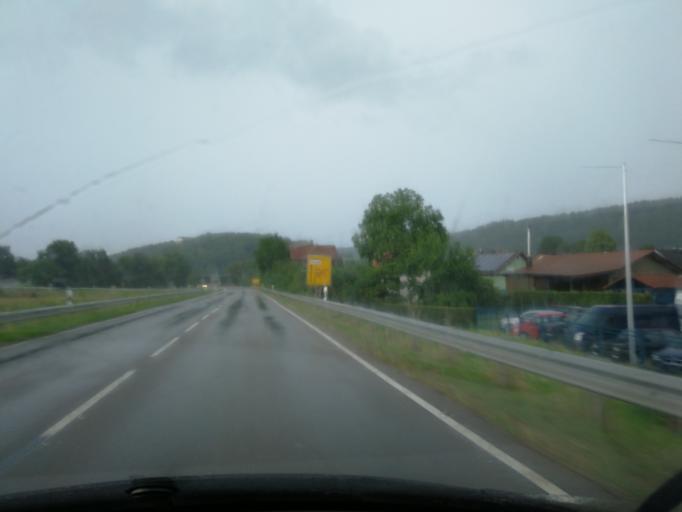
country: DE
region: Bavaria
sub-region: Upper Palatinate
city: Donaustauf
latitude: 49.0271
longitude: 12.2384
